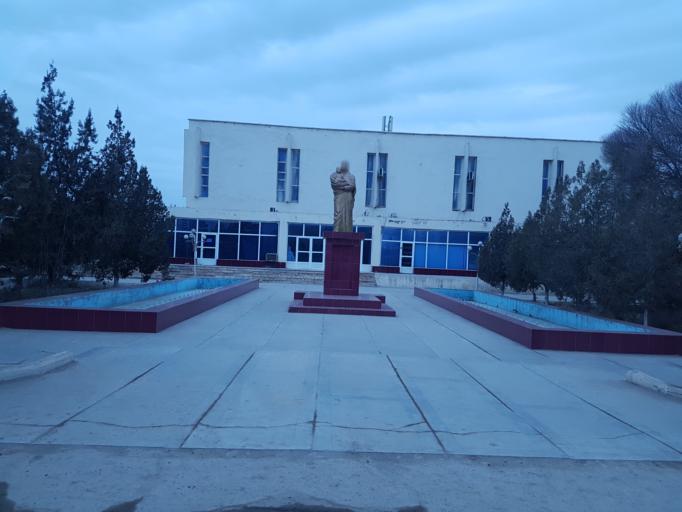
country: TM
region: Dasoguz
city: Yylanly
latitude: 41.8788
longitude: 59.6306
